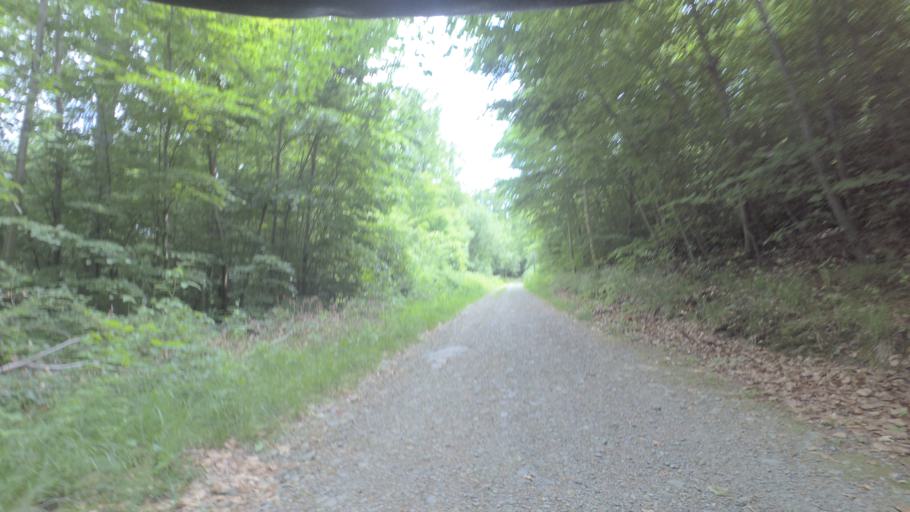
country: DE
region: Lower Saxony
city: Goslar
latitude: 51.8958
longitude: 10.4931
